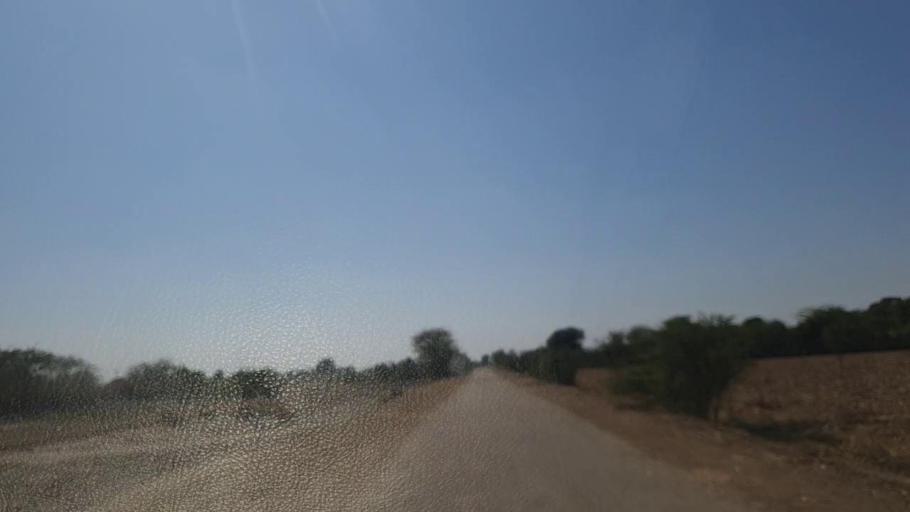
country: PK
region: Sindh
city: Naukot
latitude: 25.0587
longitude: 69.3863
